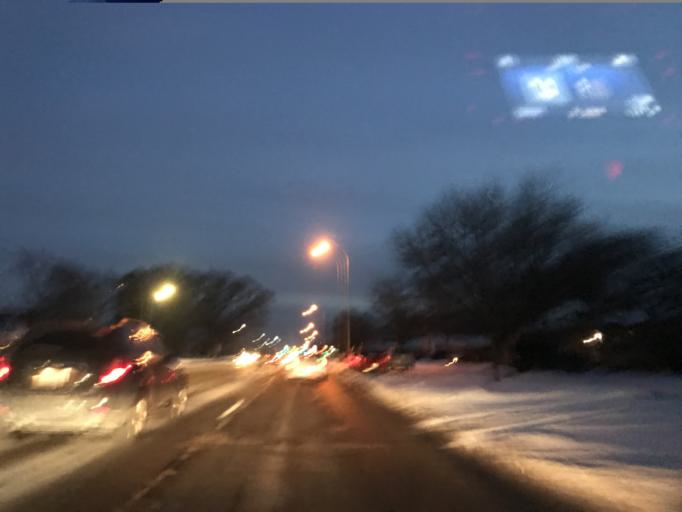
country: US
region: Michigan
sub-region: Wayne County
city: Redford
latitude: 42.3880
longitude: -83.3145
